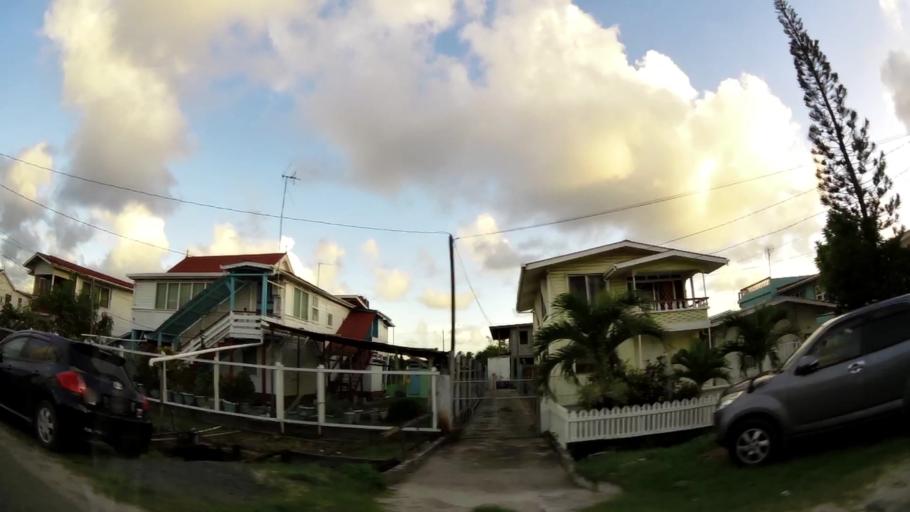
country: GY
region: Demerara-Mahaica
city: Georgetown
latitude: 6.8158
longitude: -58.1120
